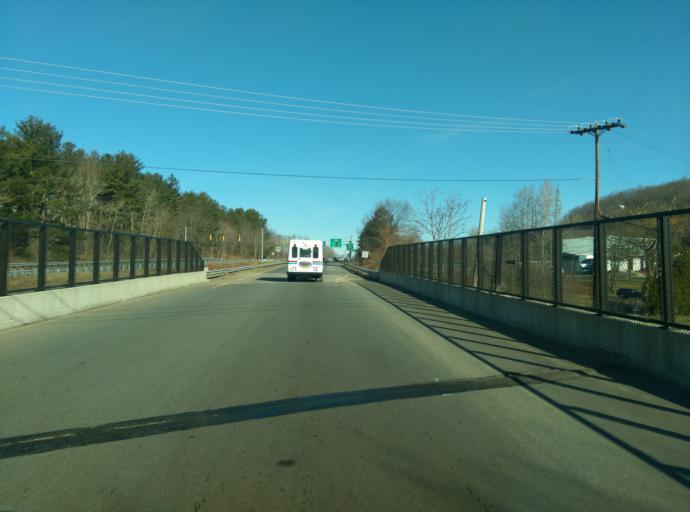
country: US
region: Massachusetts
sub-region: Essex County
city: Haverhill
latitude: 42.7511
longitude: -71.1092
